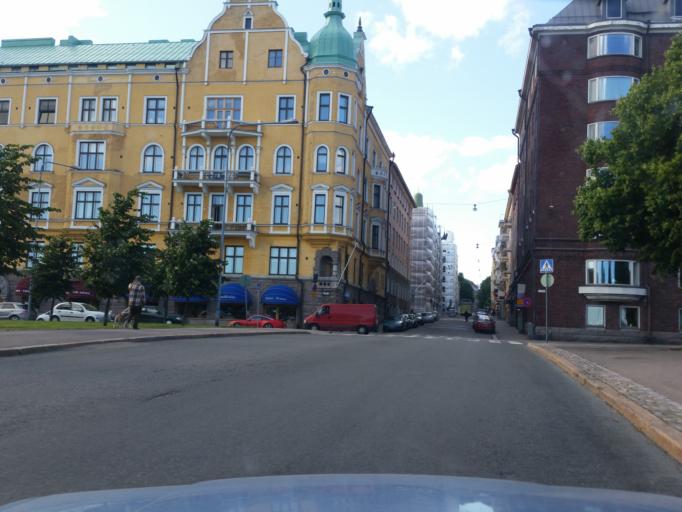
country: FI
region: Uusimaa
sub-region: Helsinki
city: Helsinki
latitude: 60.1556
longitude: 24.9506
